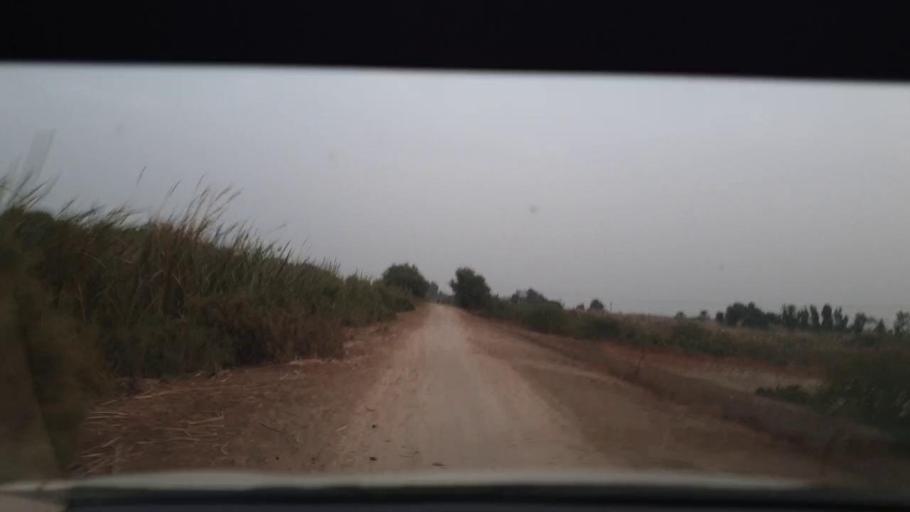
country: PK
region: Sindh
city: Berani
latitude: 25.8465
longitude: 68.7864
